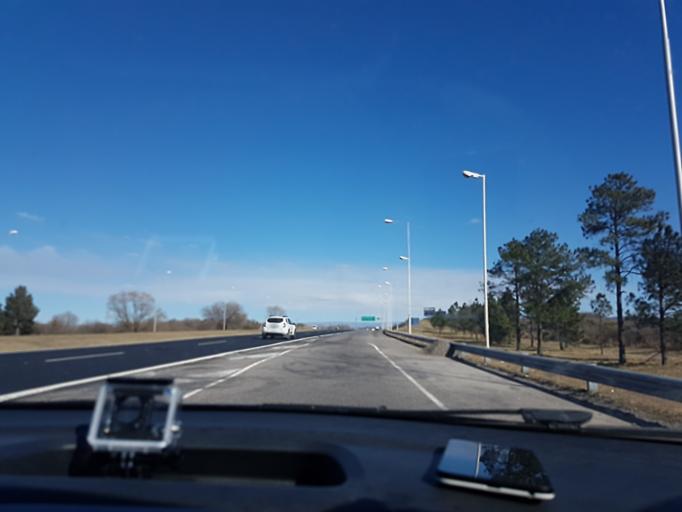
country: AR
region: Cordoba
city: Malagueno
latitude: -31.4375
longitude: -64.3281
